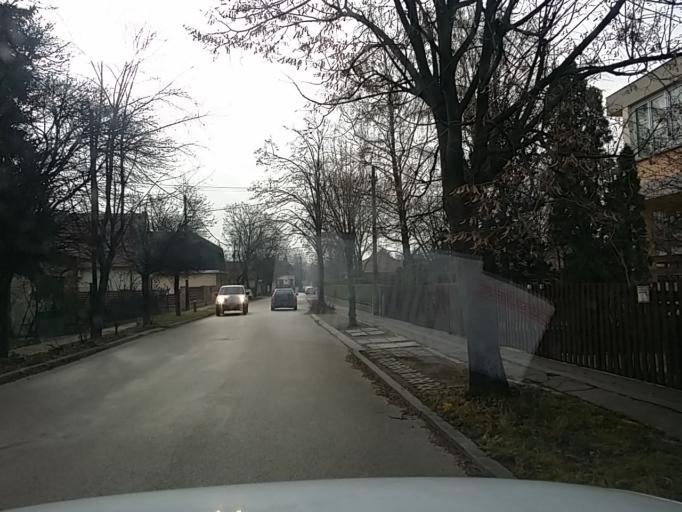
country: HU
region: Pest
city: Budakalasz
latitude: 47.5865
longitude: 19.0566
